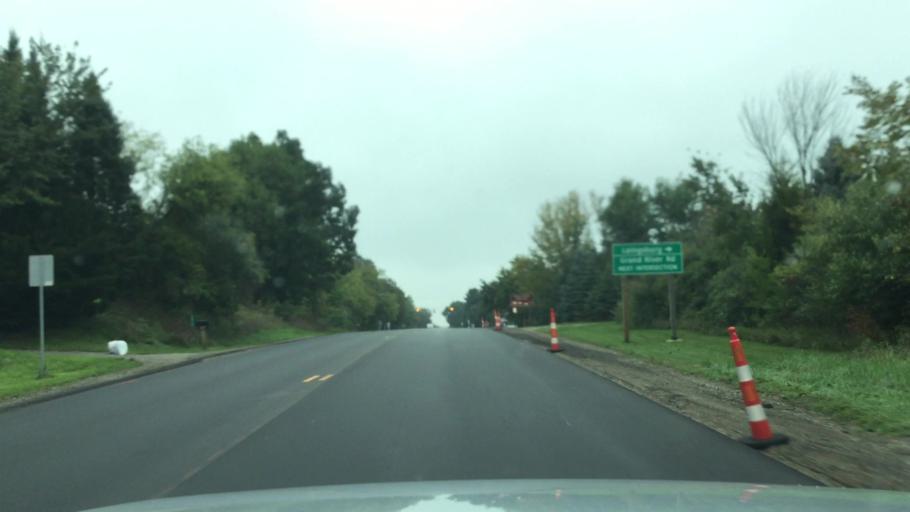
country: US
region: Michigan
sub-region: Shiawassee County
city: Perry
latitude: 42.8946
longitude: -84.2221
